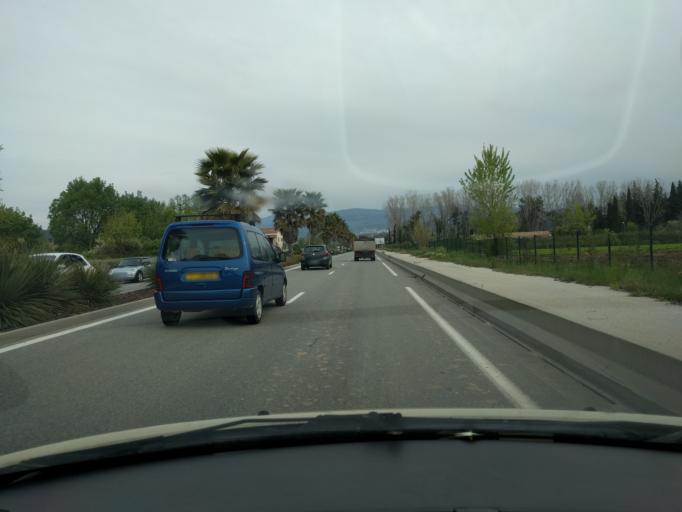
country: FR
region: Provence-Alpes-Cote d'Azur
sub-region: Departement des Alpes-Maritimes
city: Mandelieu-la-Napoule
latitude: 43.5638
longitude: 6.9499
